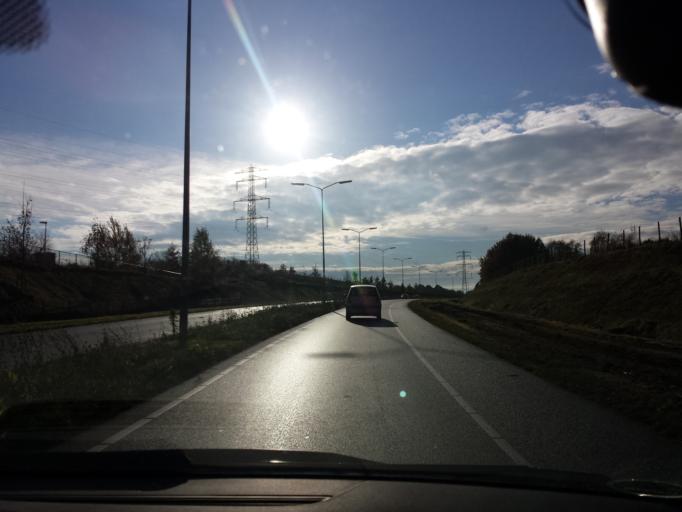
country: NL
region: Limburg
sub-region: Gemeente Heerlen
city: Heerlen
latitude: 50.8849
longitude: 6.0082
